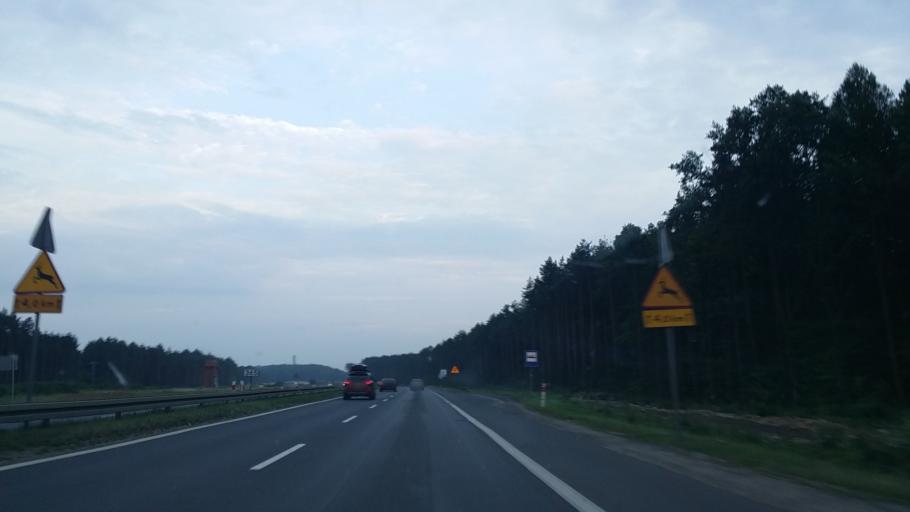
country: PL
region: Lower Silesian Voivodeship
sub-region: Powiat polkowicki
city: Polkowice
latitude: 51.4496
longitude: 16.1338
